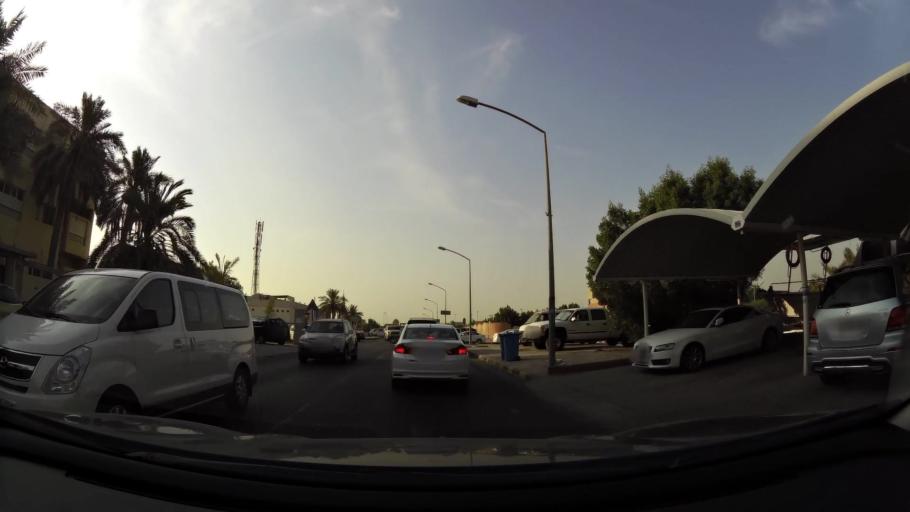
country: KW
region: Muhafazat Hawalli
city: Ar Rumaythiyah
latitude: 29.3189
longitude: 48.0767
